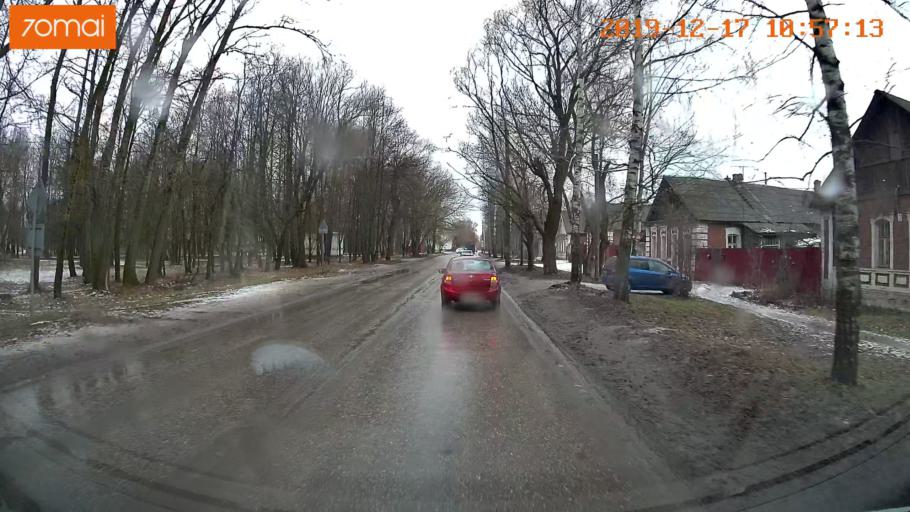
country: RU
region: Vladimir
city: Gus'-Khrustal'nyy
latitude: 55.6205
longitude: 40.6598
